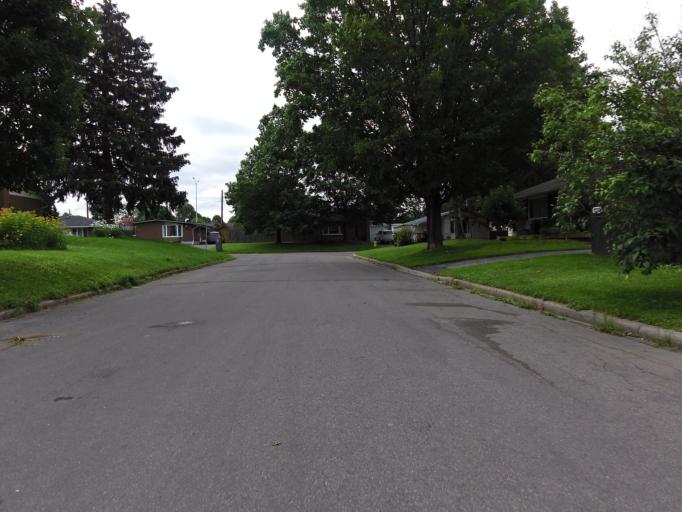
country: CA
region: Ontario
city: Bells Corners
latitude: 45.3579
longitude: -75.7769
